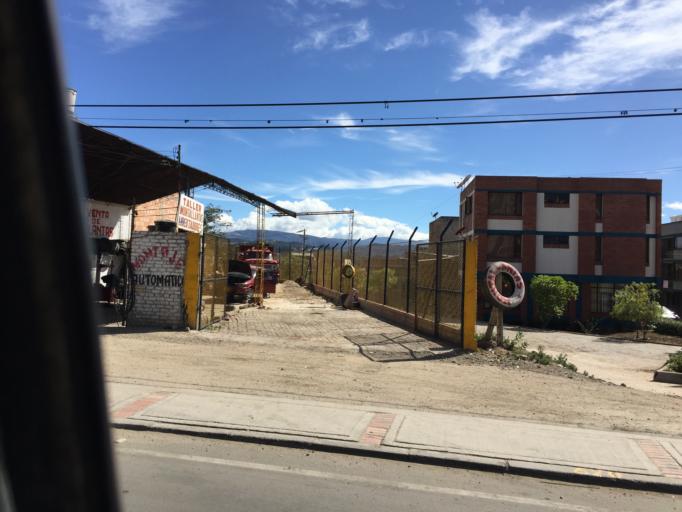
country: CO
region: Boyaca
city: Paipa
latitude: 5.7832
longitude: -73.1164
